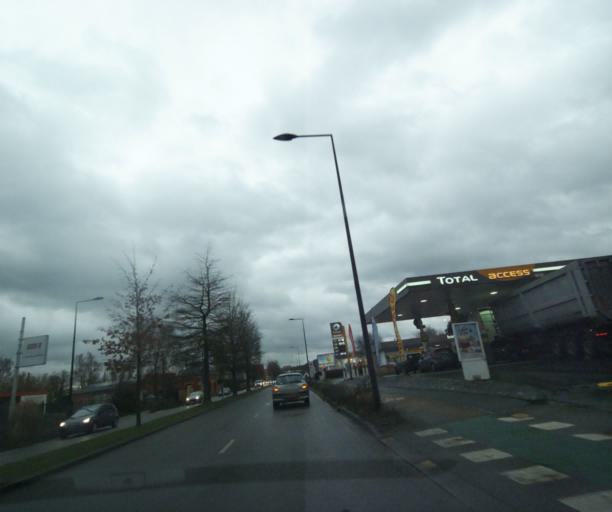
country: FR
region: Nord-Pas-de-Calais
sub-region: Departement du Nord
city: Valenciennes
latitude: 50.3694
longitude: 3.5325
